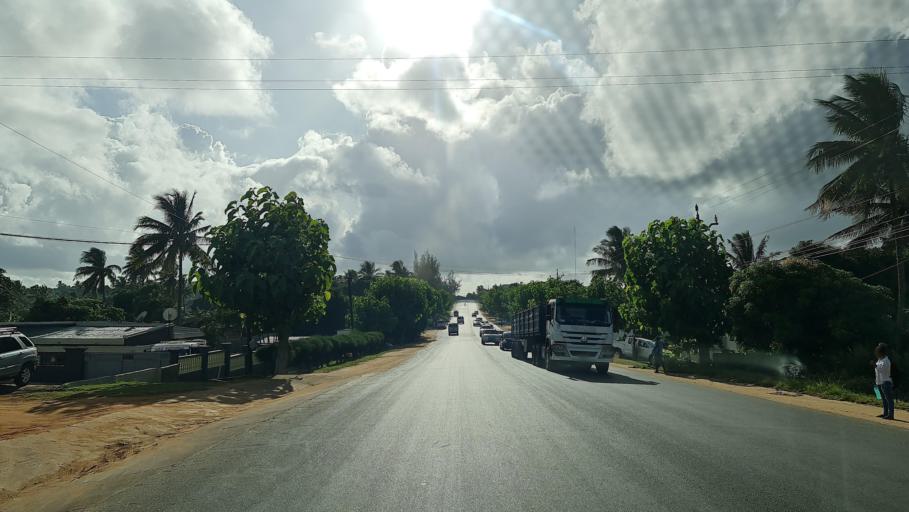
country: MZ
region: Gaza
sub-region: Xai-Xai District
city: Xai-Xai
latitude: -25.0568
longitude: 33.6567
